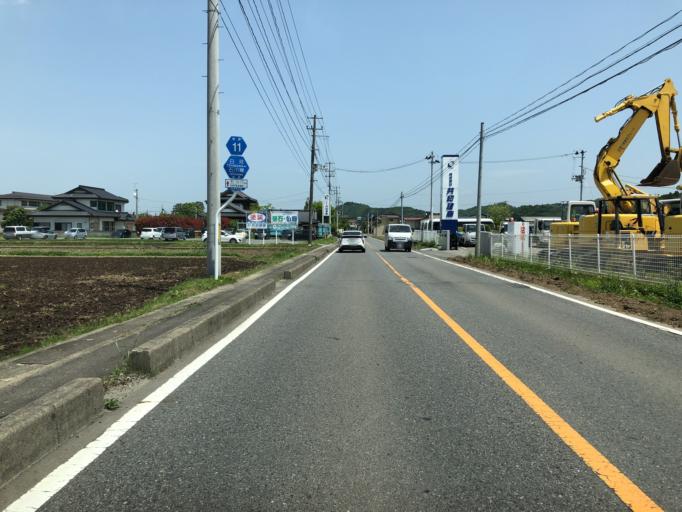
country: JP
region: Fukushima
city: Ishikawa
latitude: 37.1168
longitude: 140.2838
